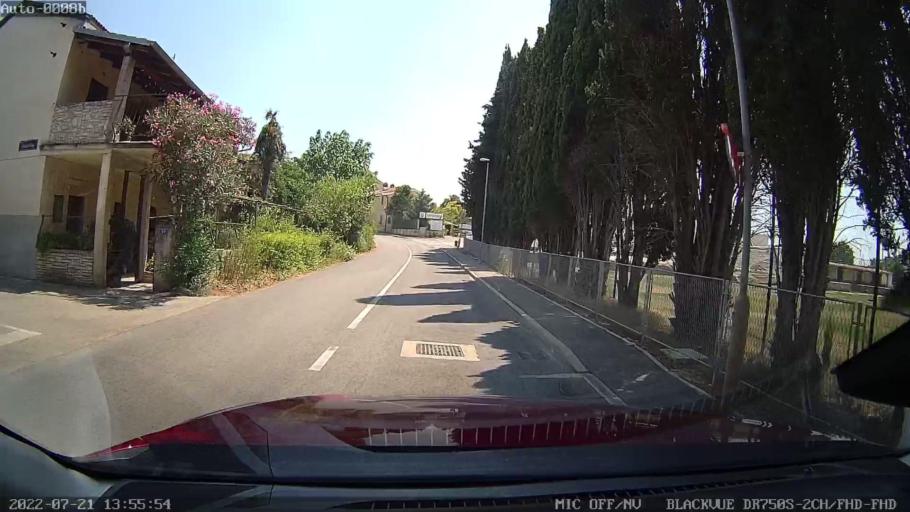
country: HR
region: Istarska
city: Pazin
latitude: 45.1216
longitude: 13.8393
